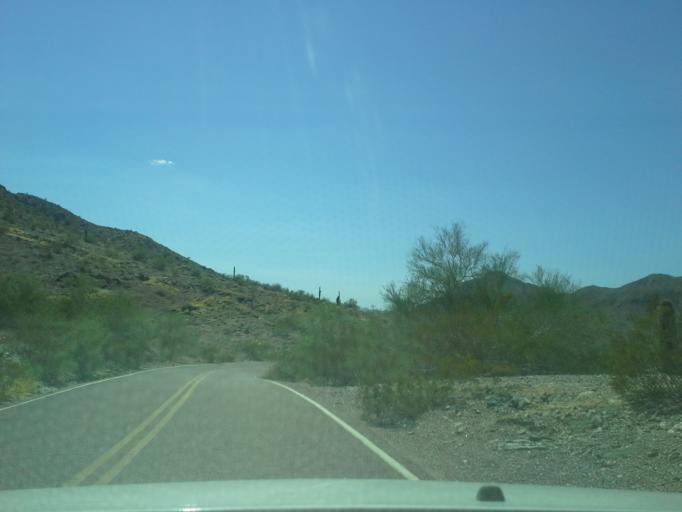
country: US
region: Arizona
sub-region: Maricopa County
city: Laveen
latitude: 33.3321
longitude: -112.0907
